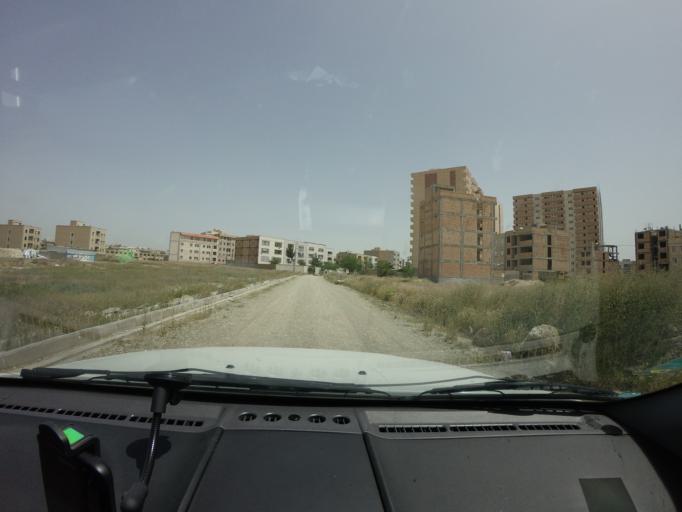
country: IR
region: Tehran
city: Eslamshahr
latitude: 35.5224
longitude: 51.2238
